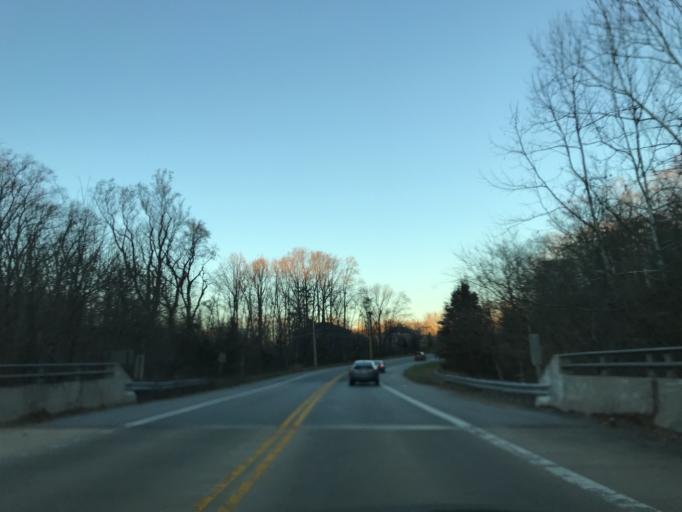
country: US
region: Maryland
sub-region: Howard County
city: Riverside
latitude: 39.2292
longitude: -76.9172
